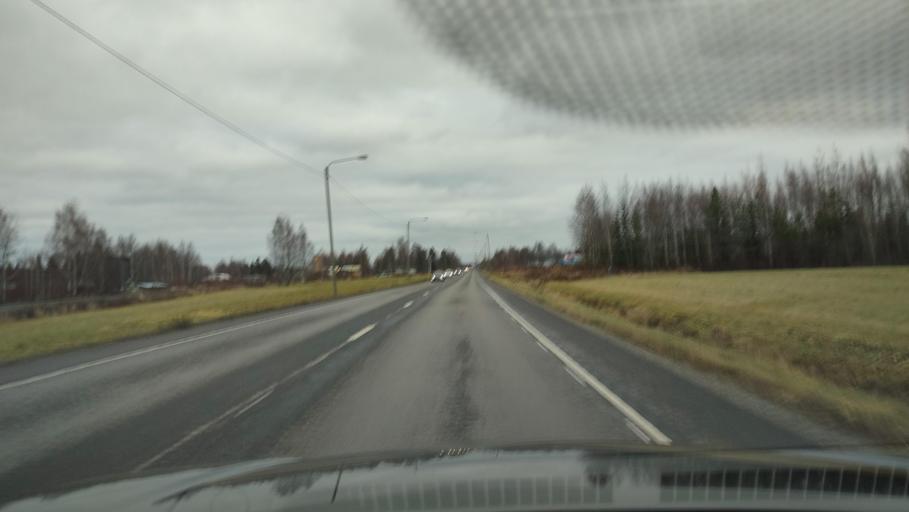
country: FI
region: Southern Ostrobothnia
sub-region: Seinaejoki
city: Ilmajoki
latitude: 62.7249
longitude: 22.5776
